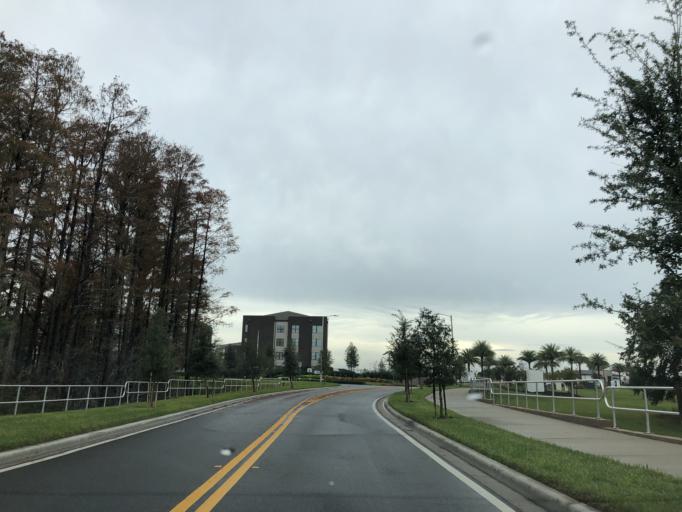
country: US
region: Florida
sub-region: Orange County
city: Doctor Phillips
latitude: 28.4459
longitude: -81.4796
